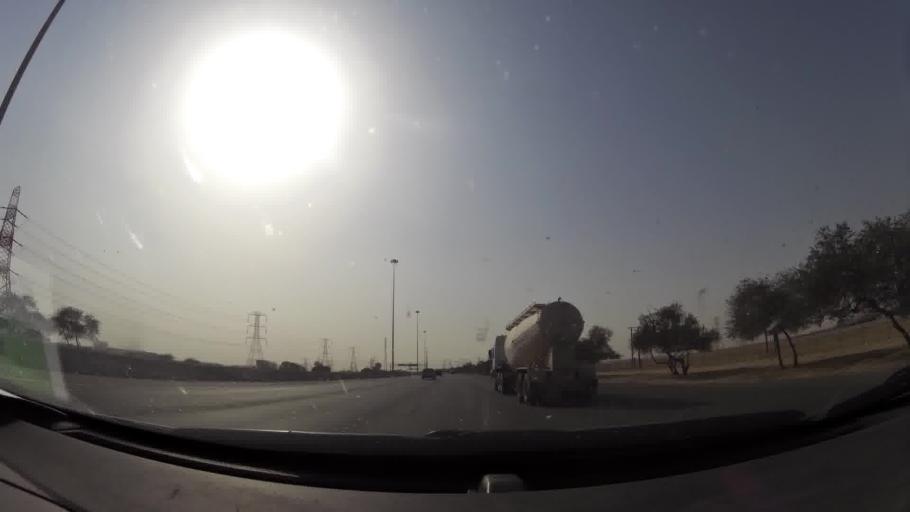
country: KW
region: Al Ahmadi
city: Al Ahmadi
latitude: 29.0258
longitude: 48.0916
